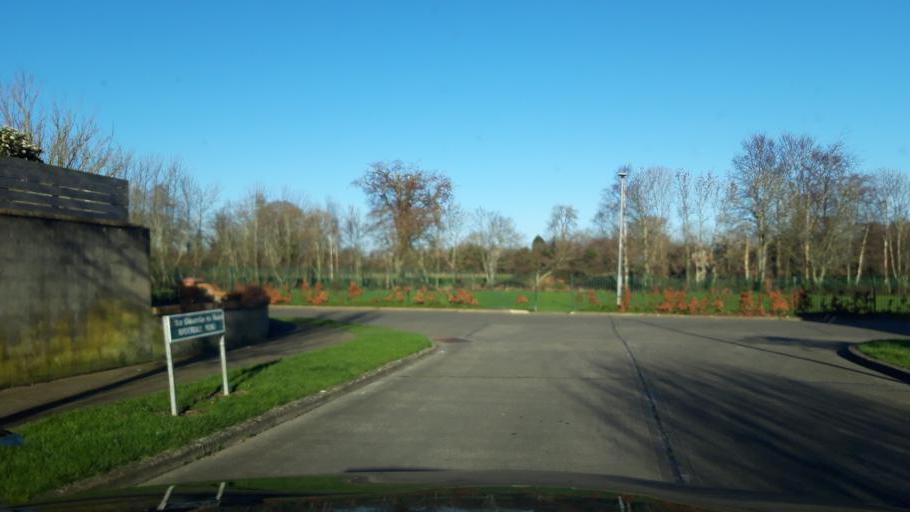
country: IE
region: Leinster
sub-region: Fingal County
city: Swords
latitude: 53.4553
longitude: -6.2486
